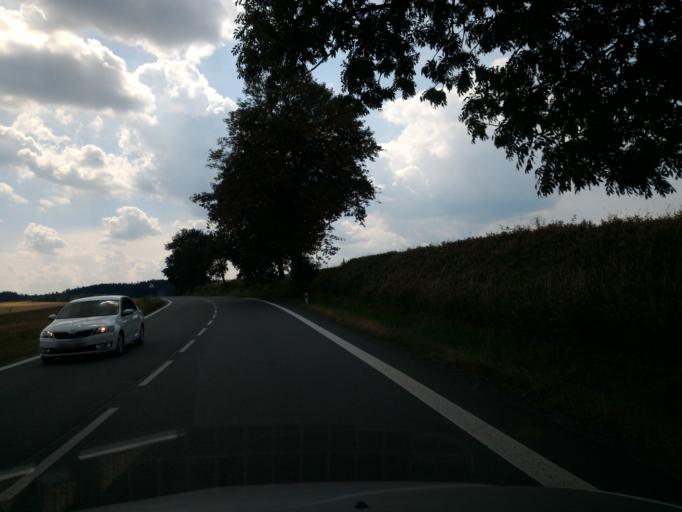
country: CZ
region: Vysocina
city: Bohdalov
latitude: 49.4794
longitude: 15.8389
